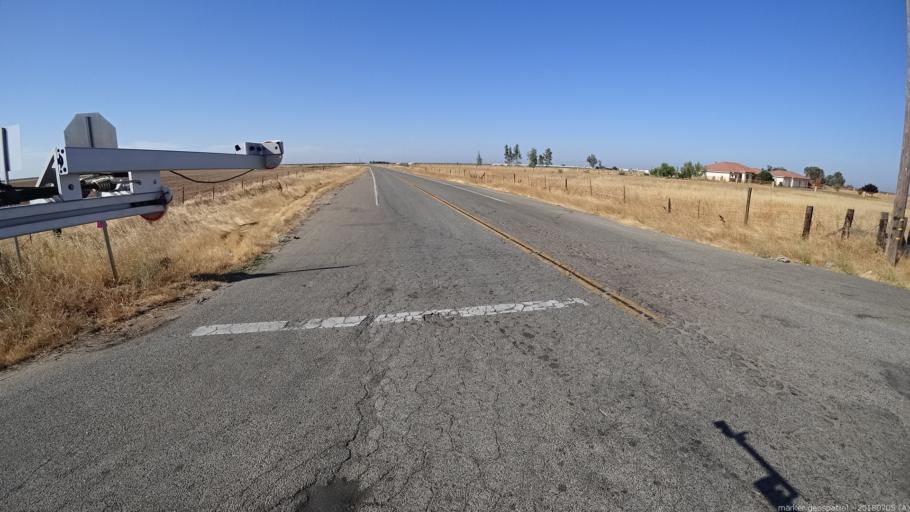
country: US
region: California
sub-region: Madera County
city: Madera Acres
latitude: 37.1272
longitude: -120.0746
